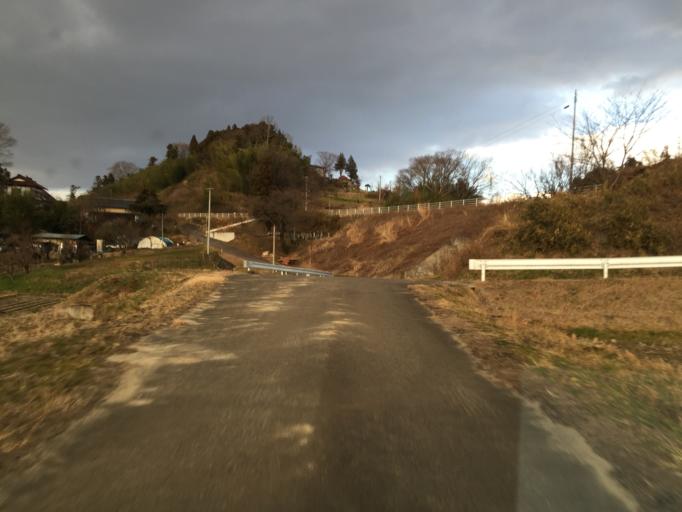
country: JP
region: Fukushima
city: Nihommatsu
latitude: 37.5556
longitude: 140.4404
